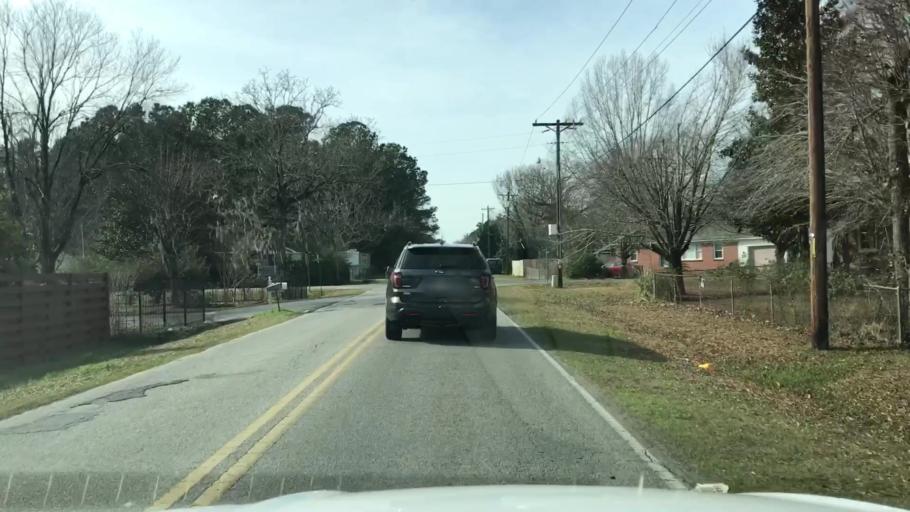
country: US
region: South Carolina
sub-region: Berkeley County
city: Goose Creek
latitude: 33.0179
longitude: -80.0316
